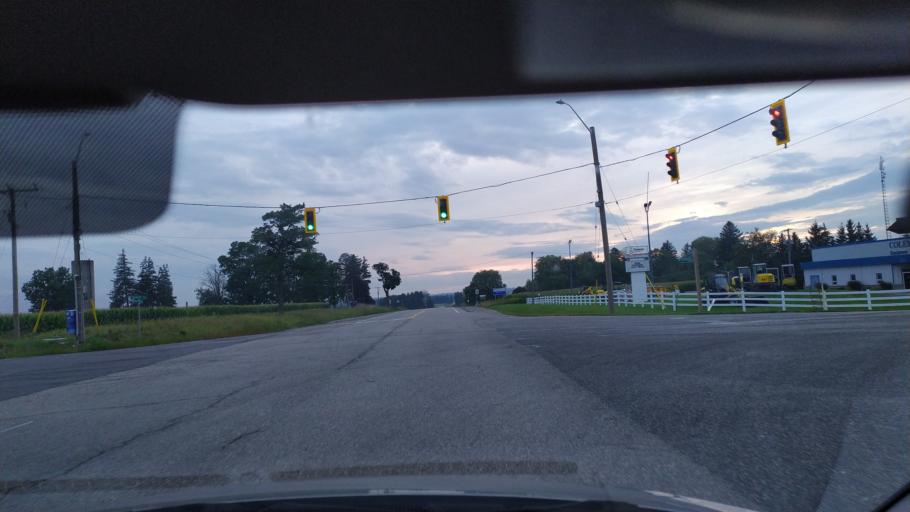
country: CA
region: Ontario
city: Kitchener
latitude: 43.3234
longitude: -80.4950
